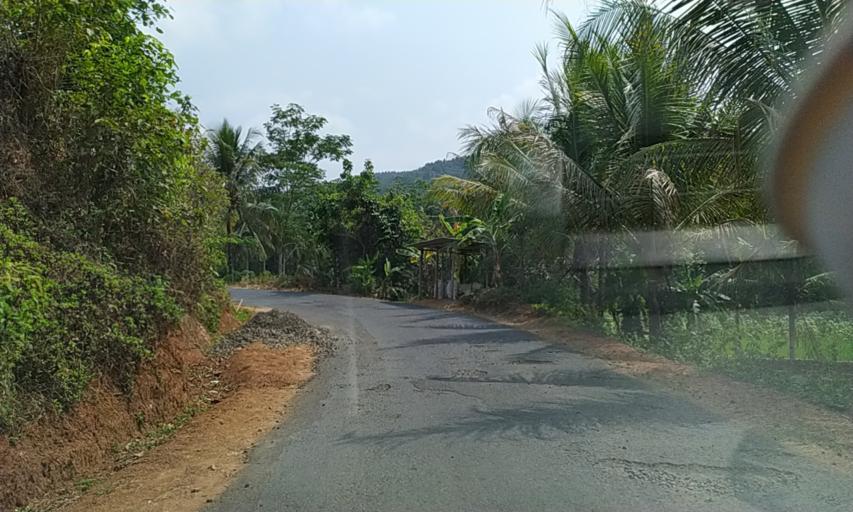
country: ID
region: Central Java
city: Cipasang
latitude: -7.2642
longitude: 108.7543
